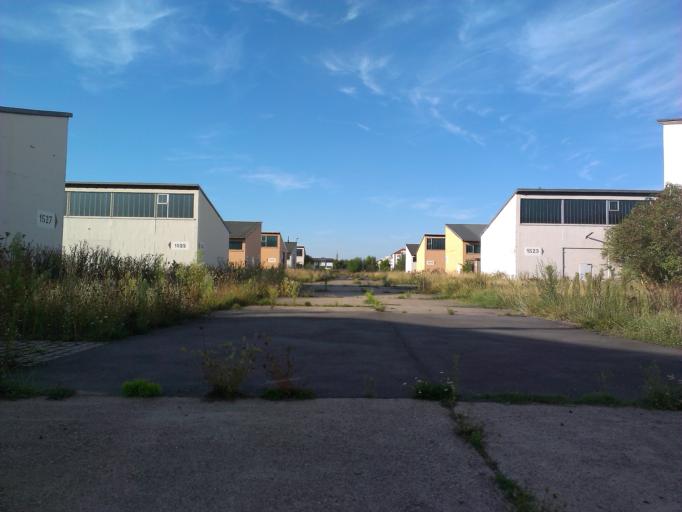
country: DE
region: Baden-Wuerttemberg
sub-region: Karlsruhe Region
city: Mannheim
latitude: 49.5001
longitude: 8.5239
